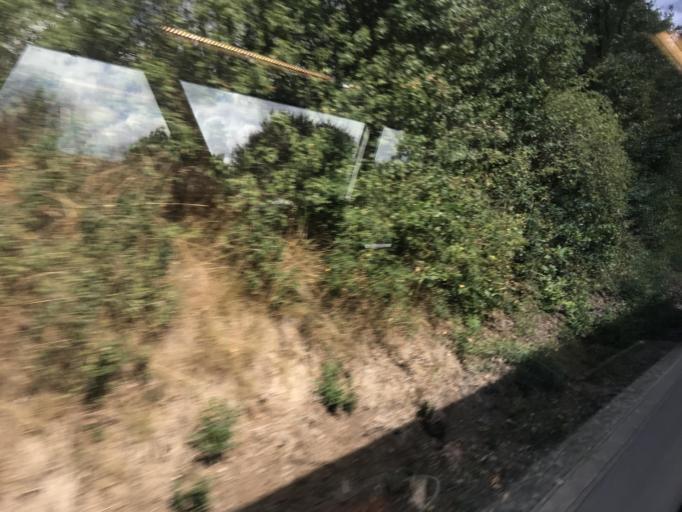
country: DE
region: Bavaria
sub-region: Regierungsbezirk Unterfranken
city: Wartmannsroth
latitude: 50.1178
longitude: 9.8026
